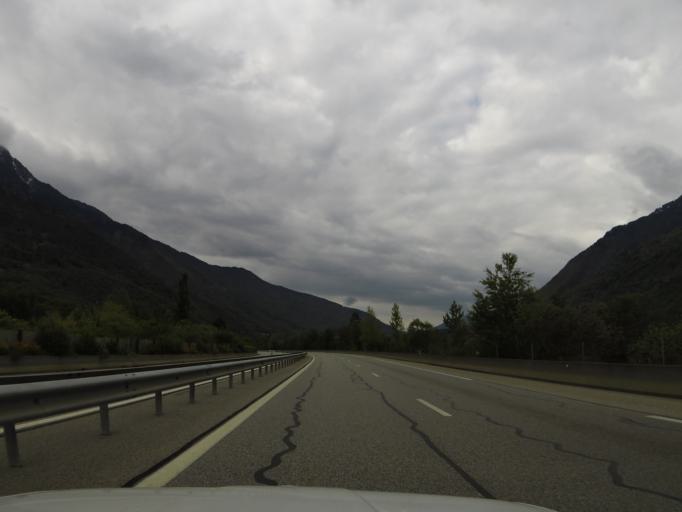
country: FR
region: Rhone-Alpes
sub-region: Departement de la Savoie
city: Saint-Remy-de-Maurienne
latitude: 45.3939
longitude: 6.2740
